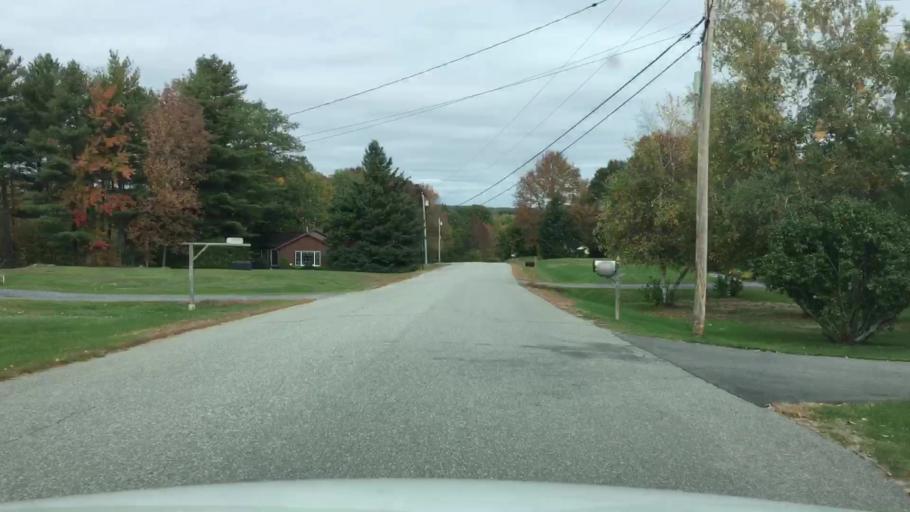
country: US
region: Maine
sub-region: Kennebec County
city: Oakland
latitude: 44.5633
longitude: -69.6806
